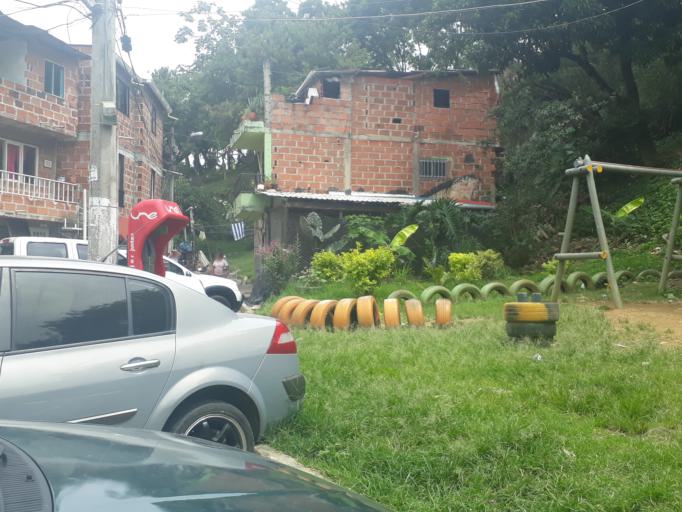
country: CO
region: Antioquia
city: Medellin
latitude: 6.2757
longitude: -75.5669
